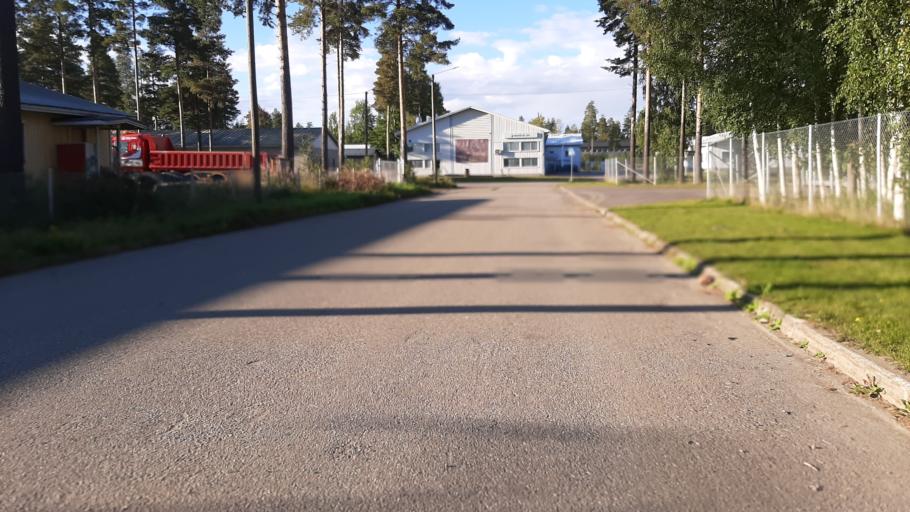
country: FI
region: North Karelia
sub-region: Joensuu
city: Joensuu
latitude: 62.6253
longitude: 29.7565
